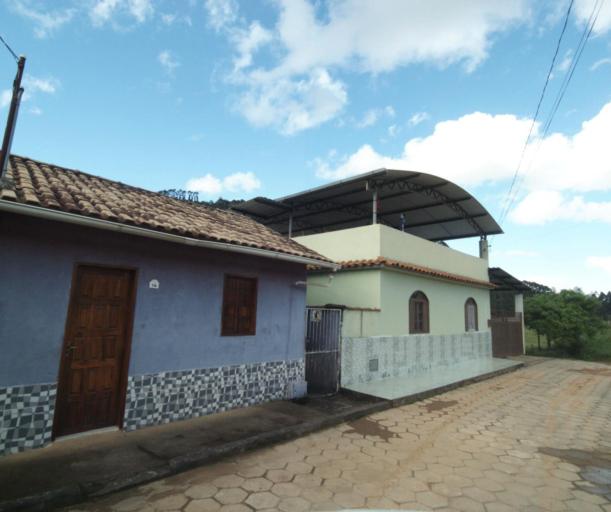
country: BR
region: Espirito Santo
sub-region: Irupi
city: Irupi
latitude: -20.5377
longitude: -41.6575
